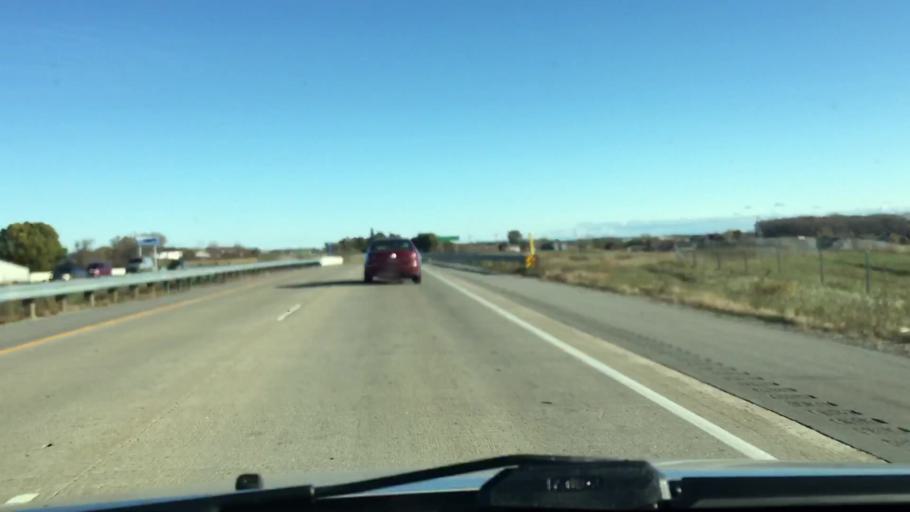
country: US
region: Wisconsin
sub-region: Brown County
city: Wrightstown
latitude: 44.3278
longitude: -88.2112
